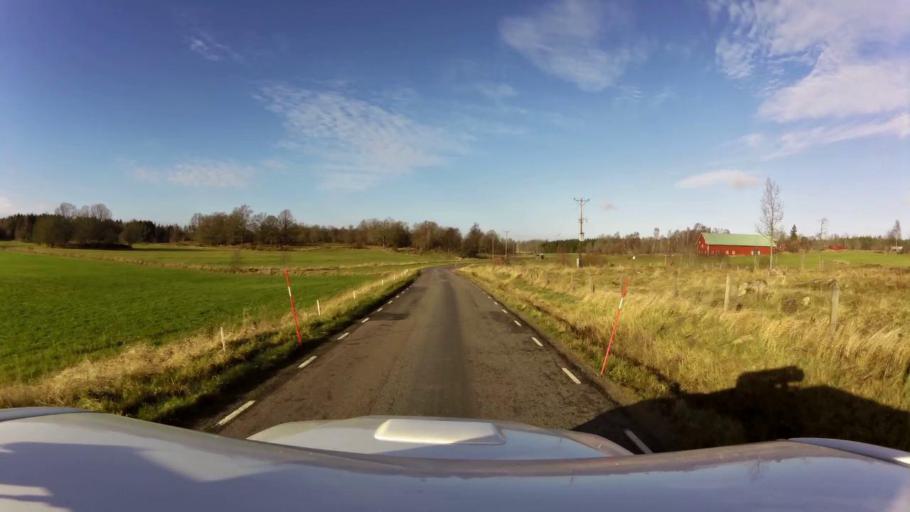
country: SE
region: OEstergoetland
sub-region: Linkopings Kommun
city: Linkoping
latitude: 58.3424
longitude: 15.6470
